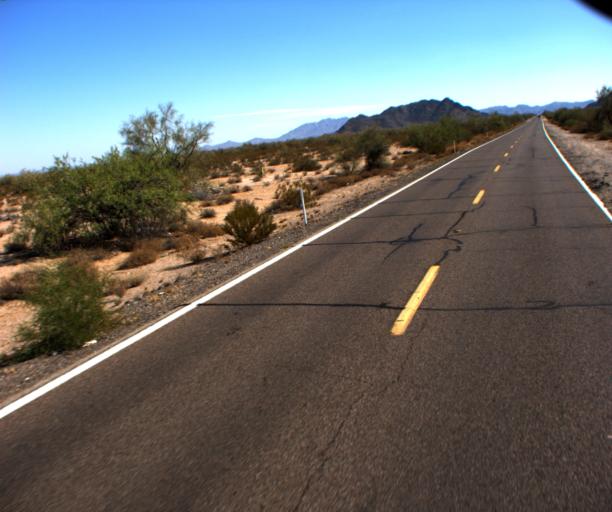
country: US
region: Arizona
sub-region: Pinal County
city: Sacaton
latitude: 33.0142
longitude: -111.7462
